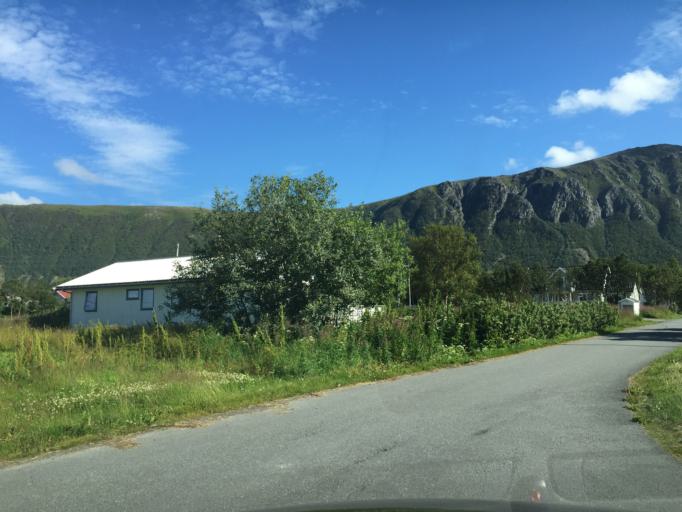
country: NO
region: Nordland
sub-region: Vagan
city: Kabelvag
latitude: 68.3923
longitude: 14.4663
